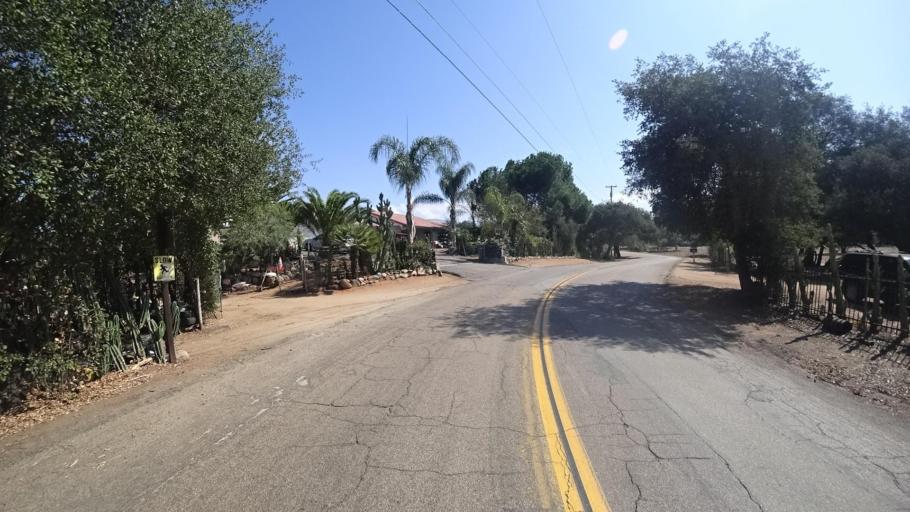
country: US
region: California
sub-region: San Diego County
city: Valley Center
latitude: 33.2921
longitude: -117.0260
